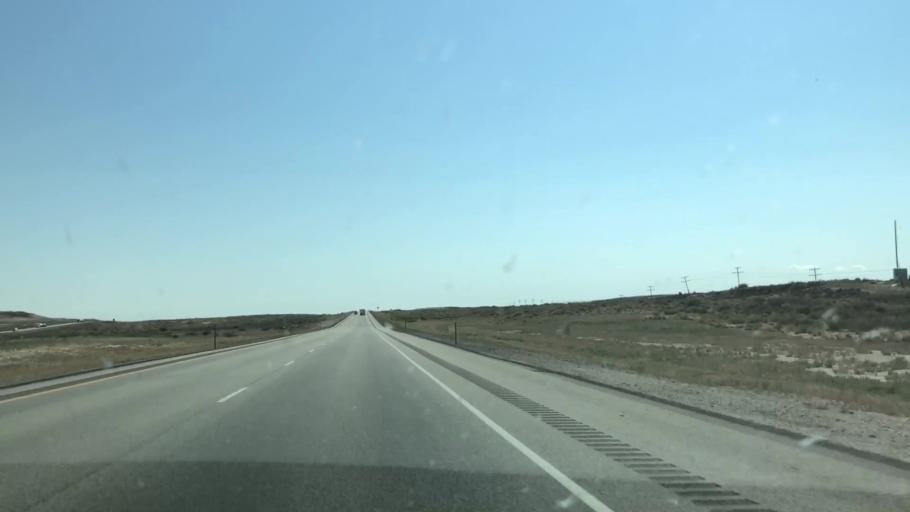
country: US
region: Wyoming
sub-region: Carbon County
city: Rawlins
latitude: 41.7052
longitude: -107.8604
